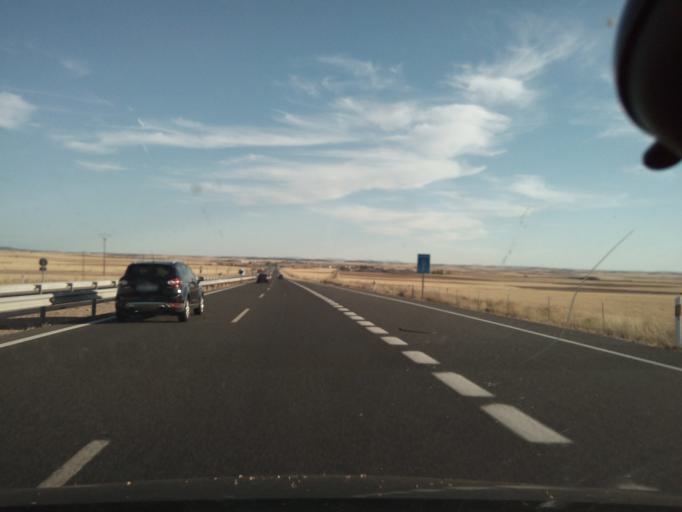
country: ES
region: Castille-La Mancha
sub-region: Province of Toledo
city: Tembleque
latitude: 39.7396
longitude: -3.4888
